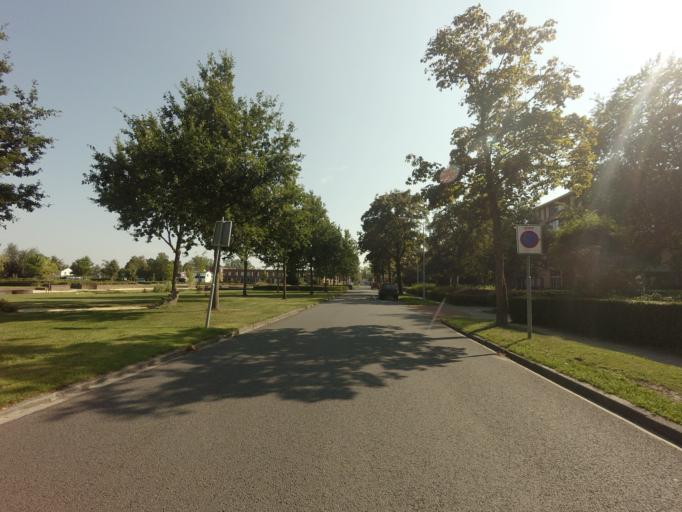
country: NL
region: Groningen
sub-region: Gemeente Zuidhorn
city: Zuidhorn
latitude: 53.2459
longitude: 6.4097
